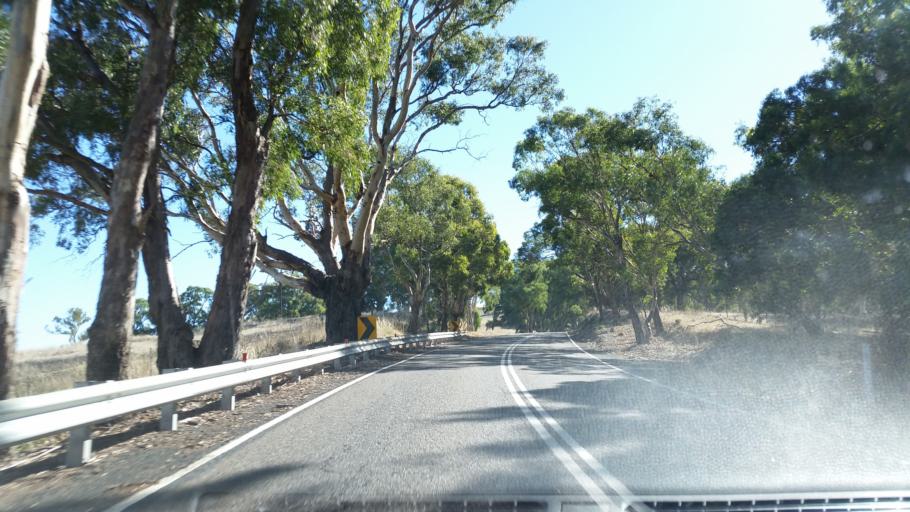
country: AU
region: South Australia
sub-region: Adelaide Hills
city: Birdwood
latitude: -34.8161
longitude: 139.0486
